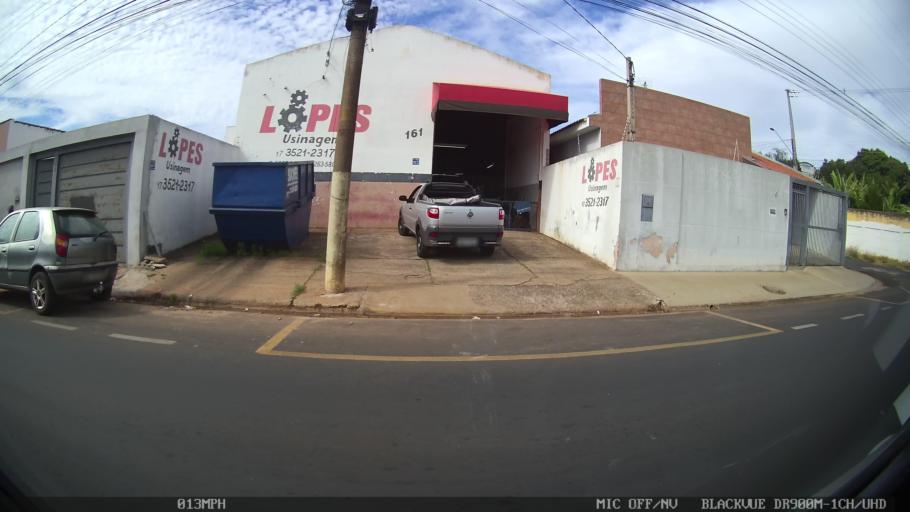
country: BR
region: Sao Paulo
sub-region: Catanduva
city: Catanduva
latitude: -21.1500
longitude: -48.9629
